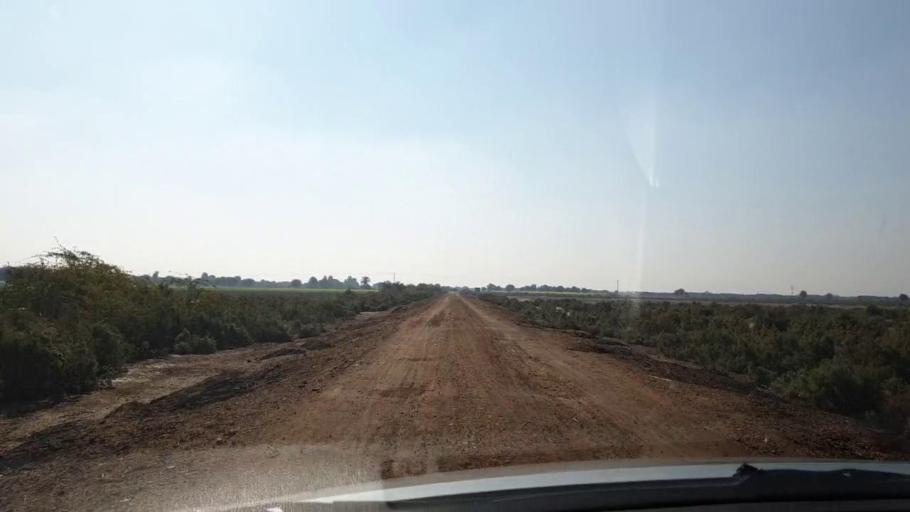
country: PK
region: Sindh
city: Jhol
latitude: 25.8735
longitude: 68.8952
